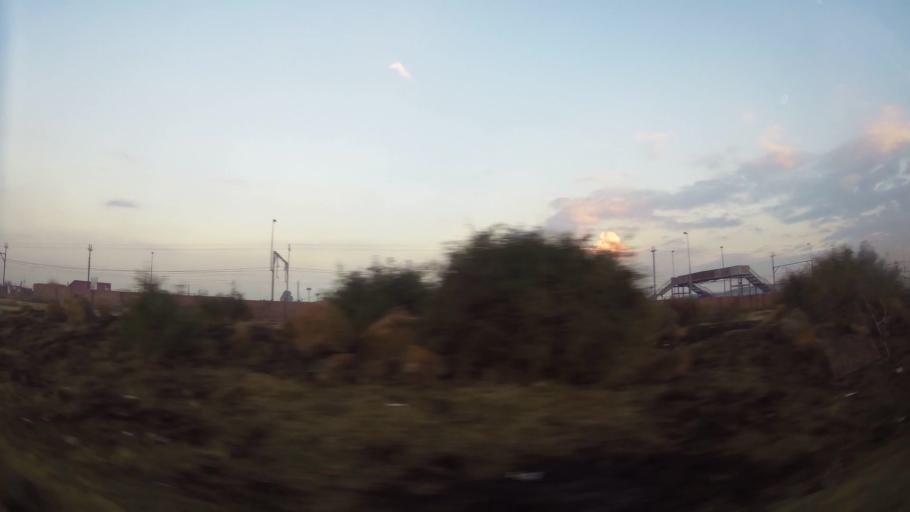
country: ZA
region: Gauteng
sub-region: City of Johannesburg Metropolitan Municipality
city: Orange Farm
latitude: -26.5569
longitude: 27.8784
